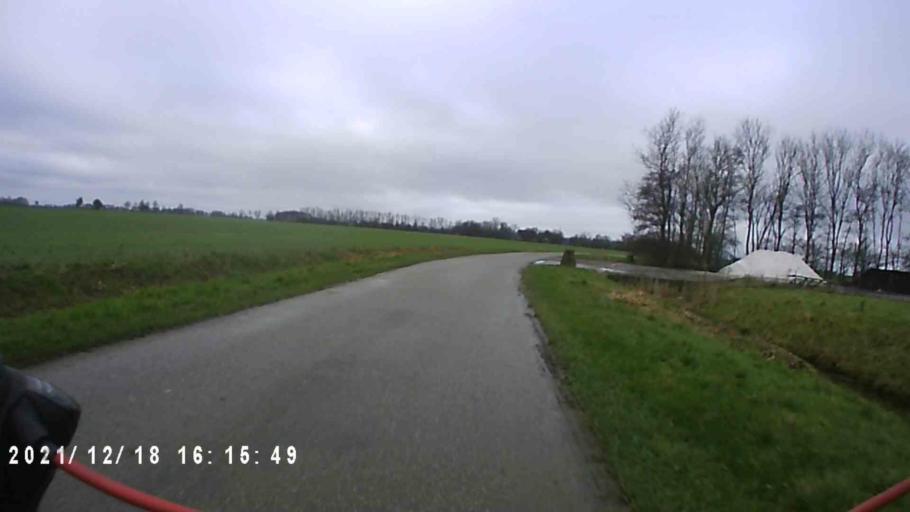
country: NL
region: Friesland
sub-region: Gemeente Dongeradeel
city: Anjum
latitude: 53.3708
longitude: 6.0603
